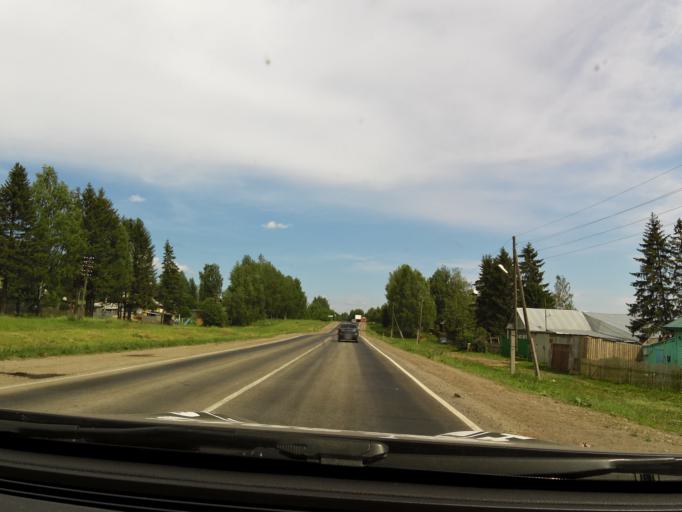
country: RU
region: Kirov
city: Vakhrushi
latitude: 58.6774
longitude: 49.9769
